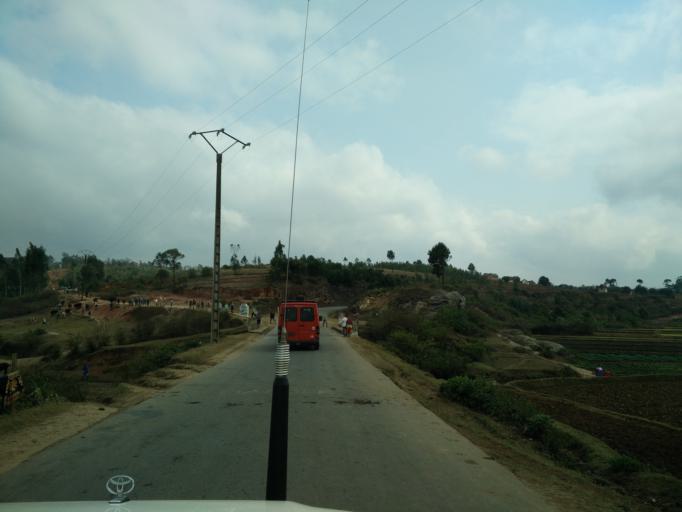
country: MG
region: Upper Matsiatra
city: Fianarantsoa
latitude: -21.3879
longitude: 47.1730
